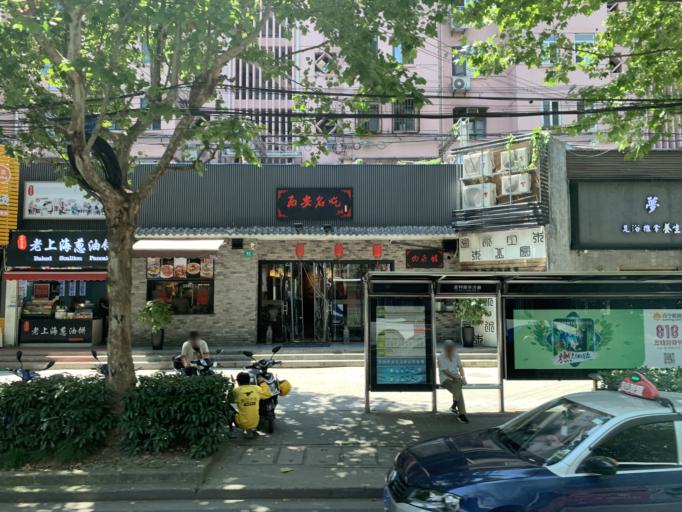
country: CN
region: Shanghai Shi
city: Huamu
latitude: 31.2137
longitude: 121.5259
